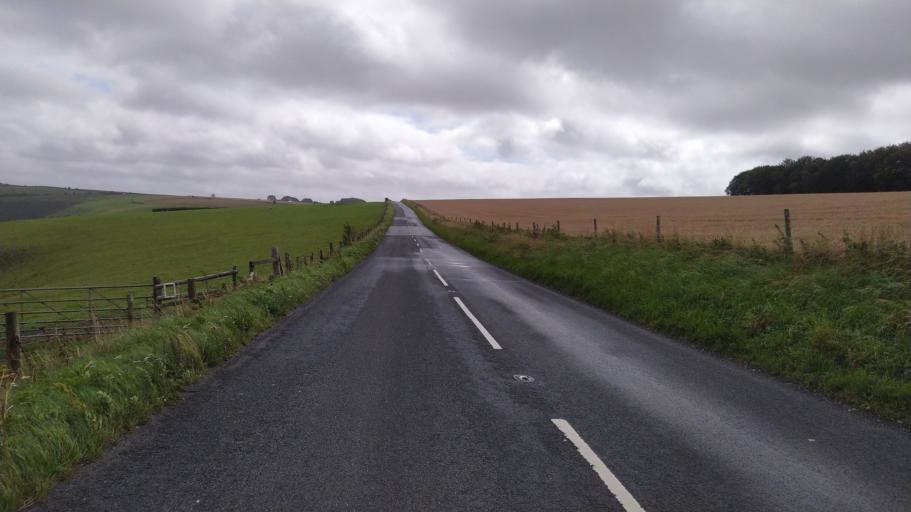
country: GB
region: England
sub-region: Dorset
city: Shaftesbury
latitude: 50.9852
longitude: -2.1413
